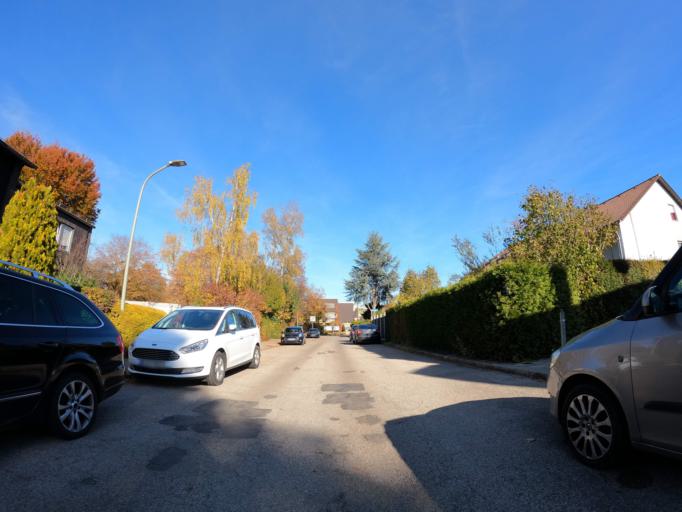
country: DE
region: Bavaria
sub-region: Upper Bavaria
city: Taufkirchen
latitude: 48.0462
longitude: 11.6027
